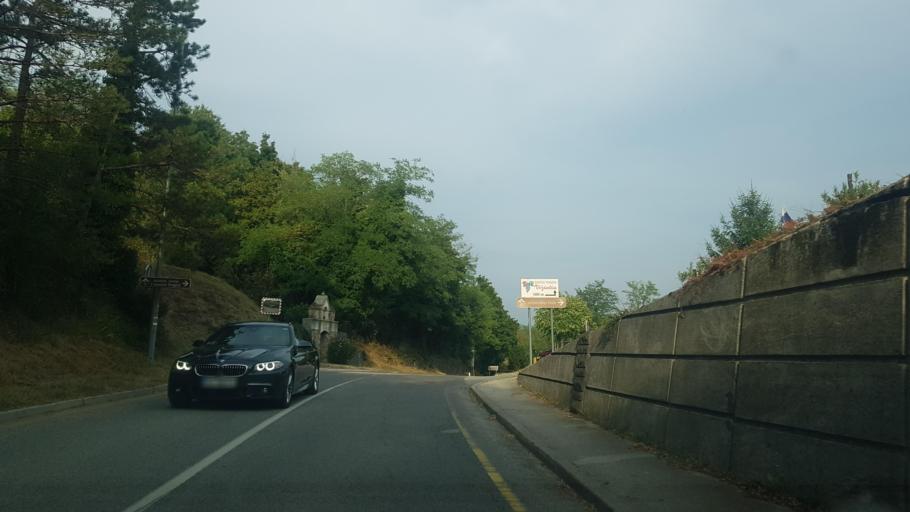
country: SI
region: Nova Gorica
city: Prvacina
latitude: 45.8876
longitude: 13.7503
